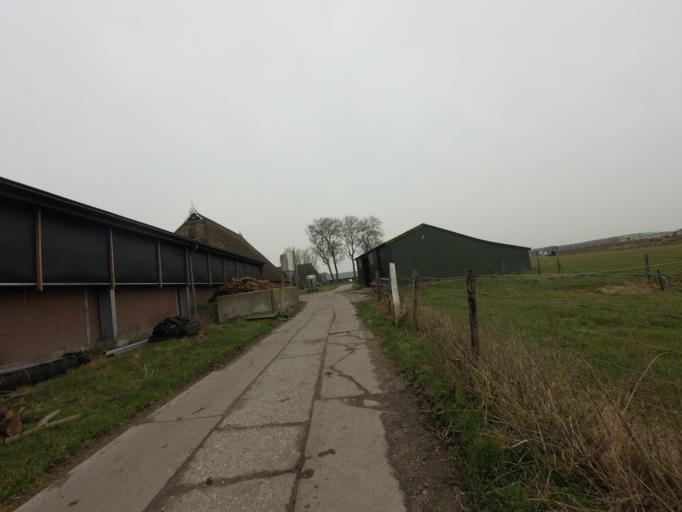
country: NL
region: Friesland
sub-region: Gemeente Franekeradeel
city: Franeker
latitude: 53.1934
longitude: 5.5537
